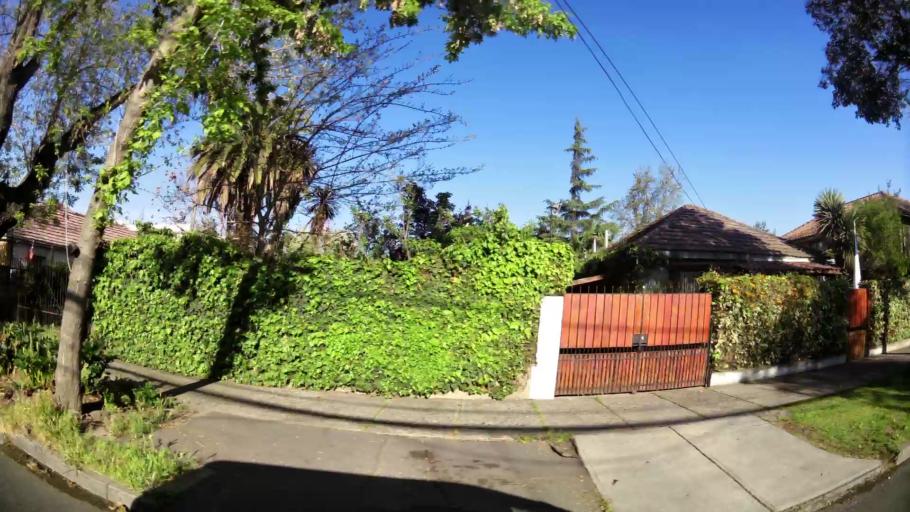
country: CL
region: Santiago Metropolitan
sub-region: Provincia de Santiago
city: Villa Presidente Frei, Nunoa, Santiago, Chile
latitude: -33.4505
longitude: -70.5674
